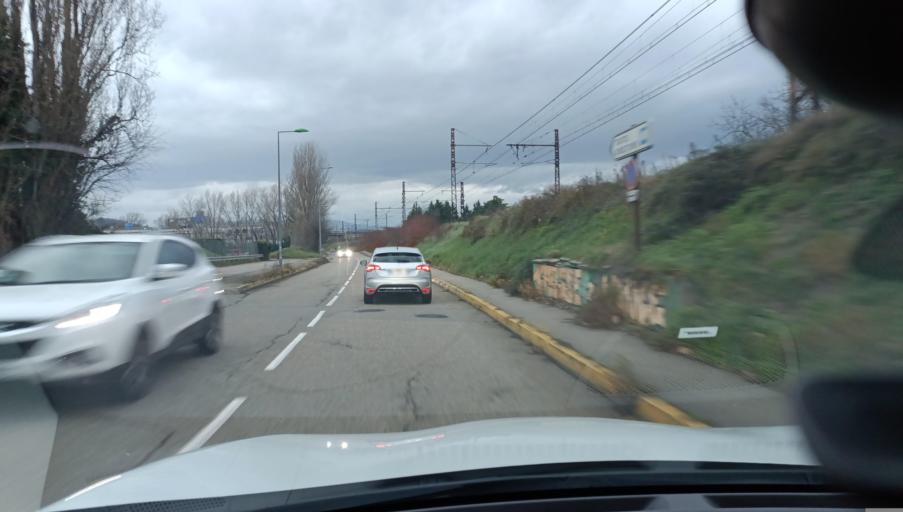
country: FR
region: Rhone-Alpes
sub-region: Departement de l'Isere
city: Chasse-sur-Rhone
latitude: 45.5766
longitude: 4.8092
